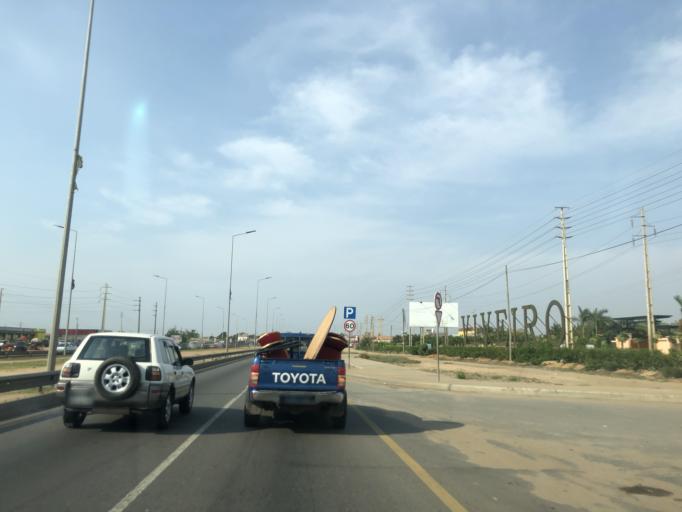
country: AO
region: Luanda
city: Luanda
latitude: -8.9432
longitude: 13.2610
